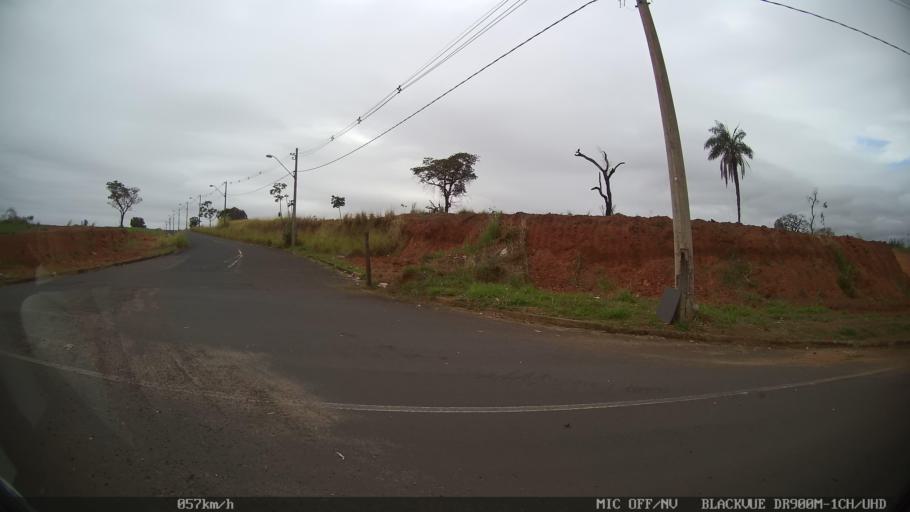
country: BR
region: Sao Paulo
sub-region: Sao Jose Do Rio Preto
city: Sao Jose do Rio Preto
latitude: -20.8280
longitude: -49.4303
